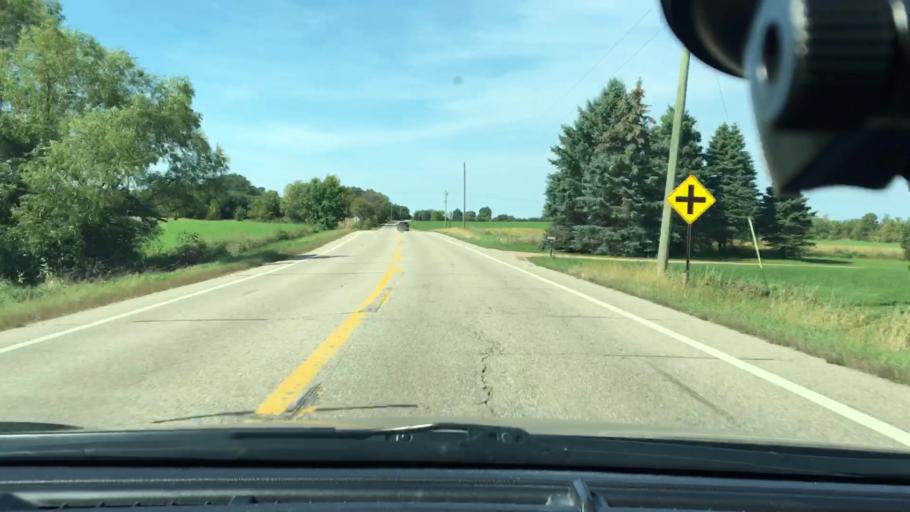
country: US
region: Minnesota
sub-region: Hennepin County
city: Corcoran
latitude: 45.1206
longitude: -93.6031
